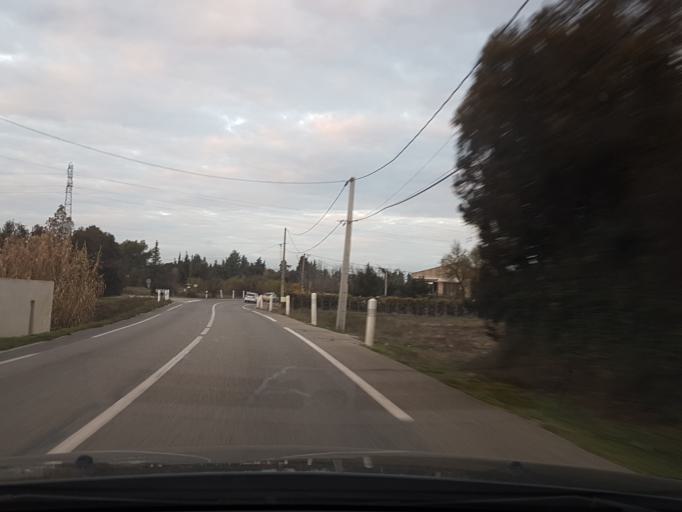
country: FR
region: Provence-Alpes-Cote d'Azur
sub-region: Departement du Vaucluse
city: Monteux
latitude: 44.0505
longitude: 4.9989
